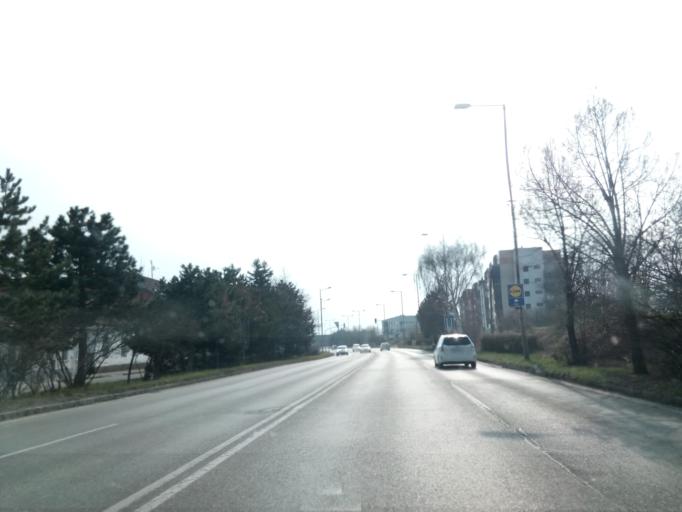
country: SK
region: Trenciansky
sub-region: Okres Trencin
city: Trencin
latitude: 48.8916
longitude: 18.0315
